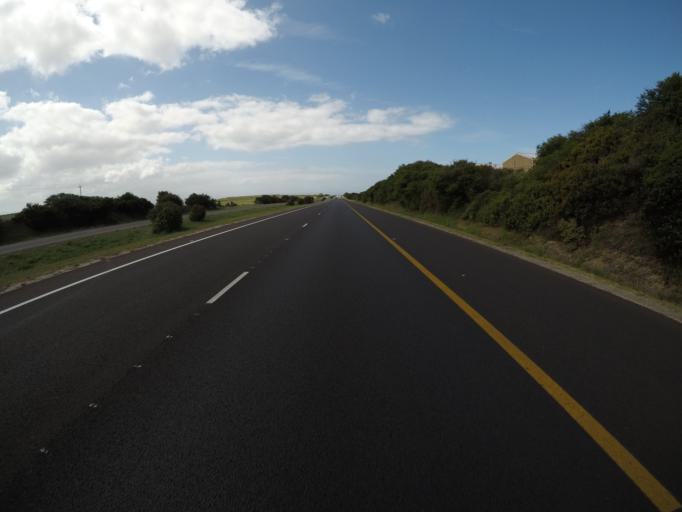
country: ZA
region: Western Cape
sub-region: Eden District Municipality
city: Mossel Bay
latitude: -34.1678
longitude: 22.0814
